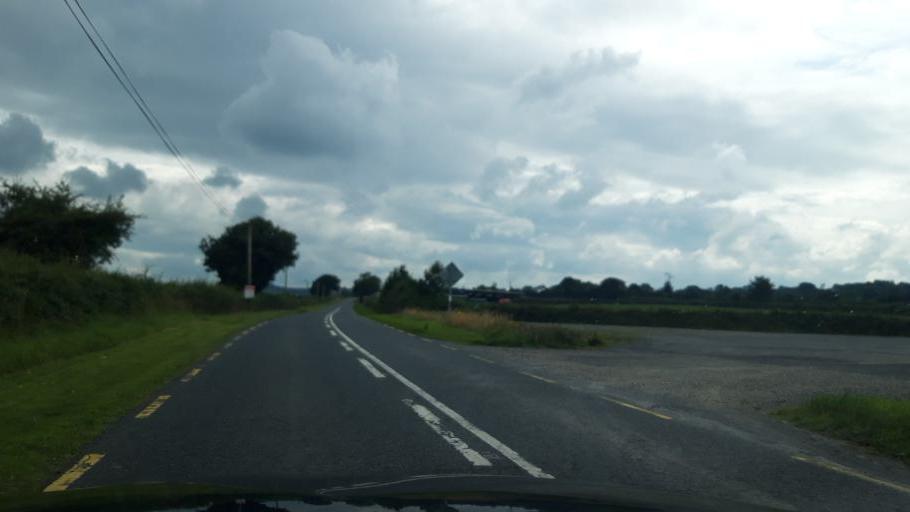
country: IE
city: Ballylinan
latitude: 52.9225
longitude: -7.0623
